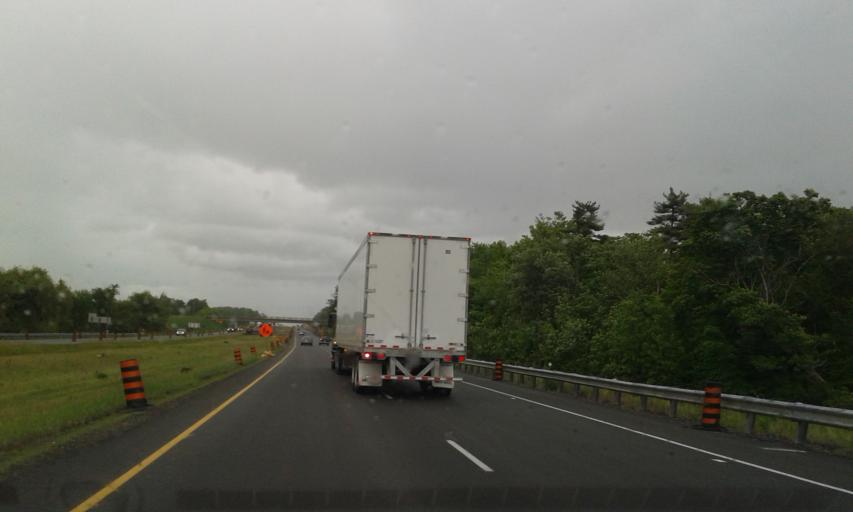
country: CA
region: Ontario
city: Gananoque
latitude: 44.3526
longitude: -76.1009
